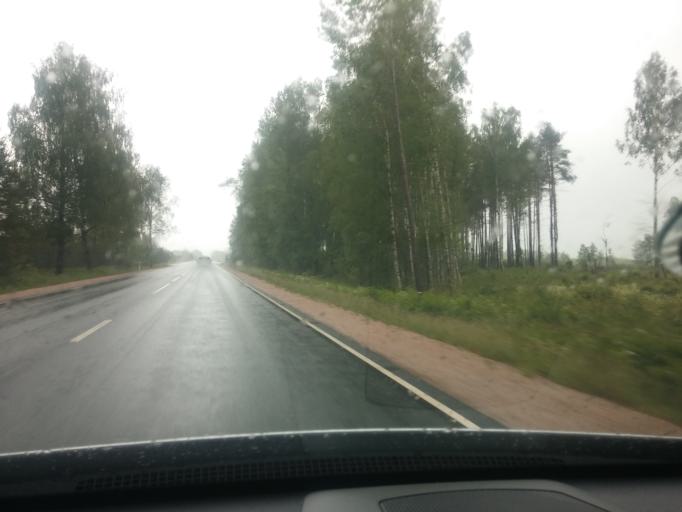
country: LV
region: Ikskile
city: Ikskile
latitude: 56.8867
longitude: 24.4909
